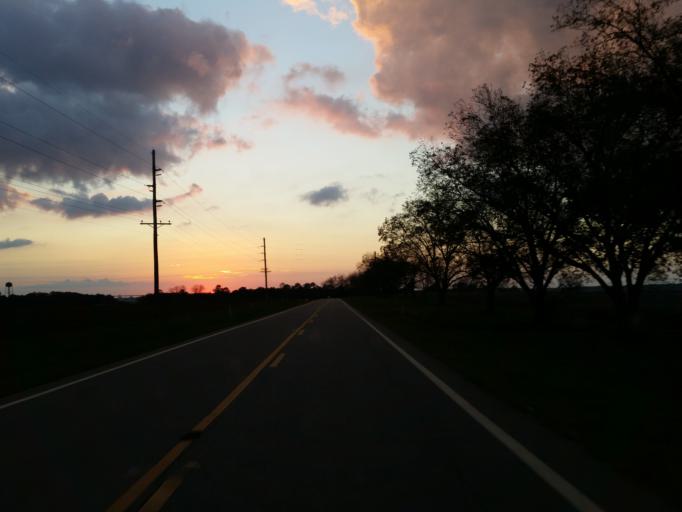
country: US
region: Georgia
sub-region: Dooly County
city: Vienna
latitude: 32.1314
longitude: -83.7021
